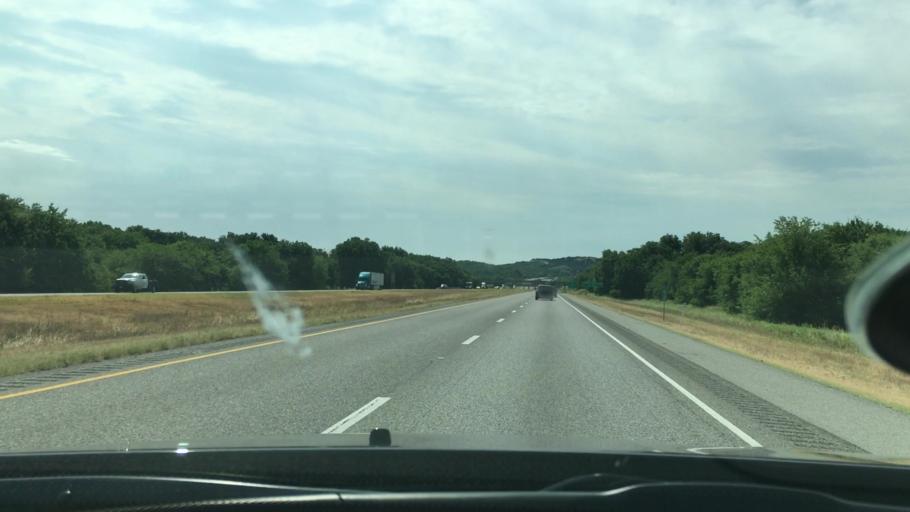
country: US
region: Oklahoma
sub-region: Murray County
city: Davis
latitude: 34.4603
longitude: -97.1449
